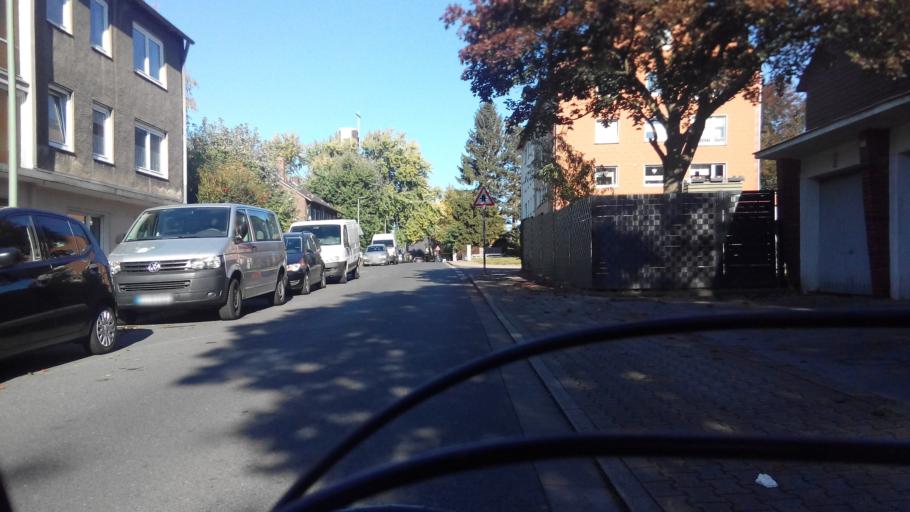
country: DE
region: North Rhine-Westphalia
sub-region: Regierungsbezirk Munster
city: Gelsenkirchen
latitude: 51.4963
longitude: 7.1330
